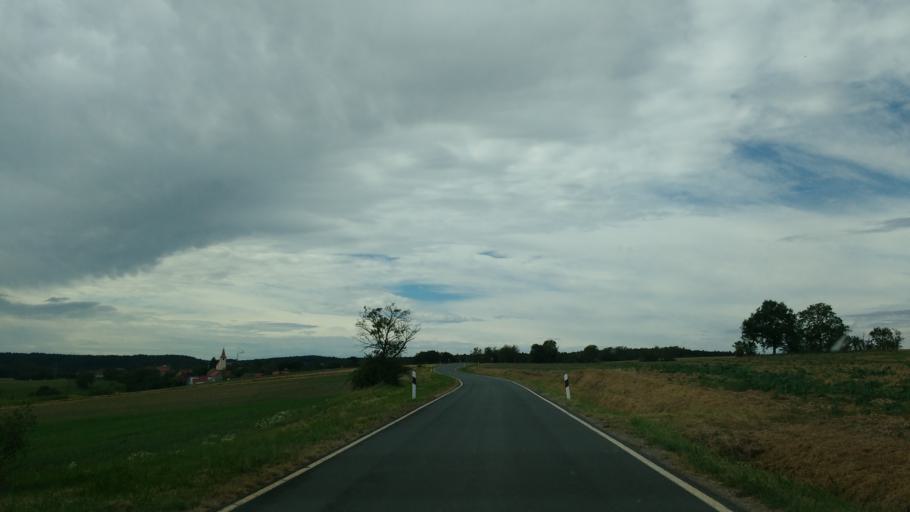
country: DE
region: Bavaria
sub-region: Regierungsbezirk Unterfranken
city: Geiselwind
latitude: 49.8005
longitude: 10.4989
